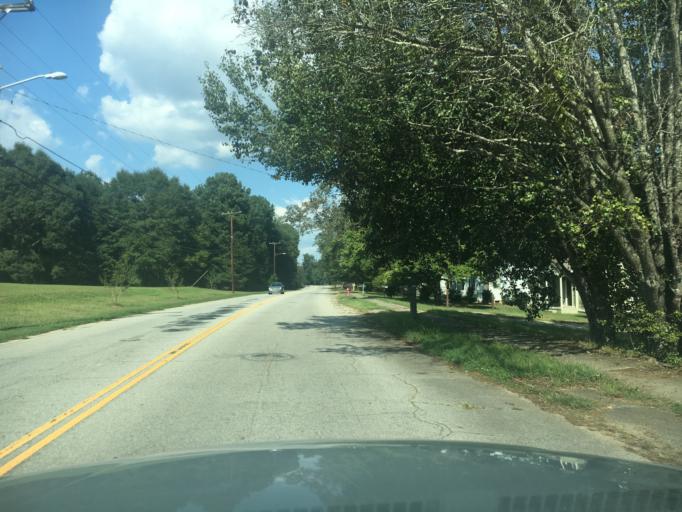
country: US
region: South Carolina
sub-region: Anderson County
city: Pendleton
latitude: 34.6582
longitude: -82.7725
